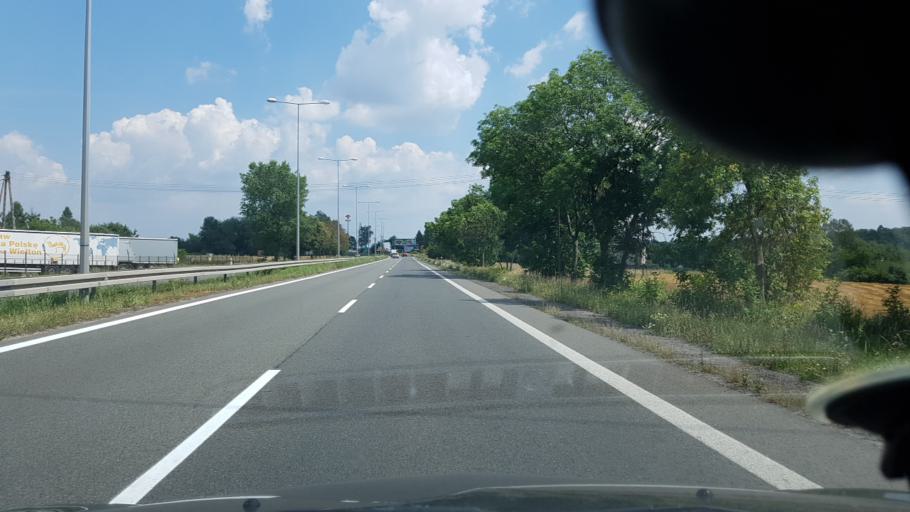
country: PL
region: Silesian Voivodeship
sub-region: Powiat mikolowski
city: Laziska Gorne
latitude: 50.1695
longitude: 18.8632
